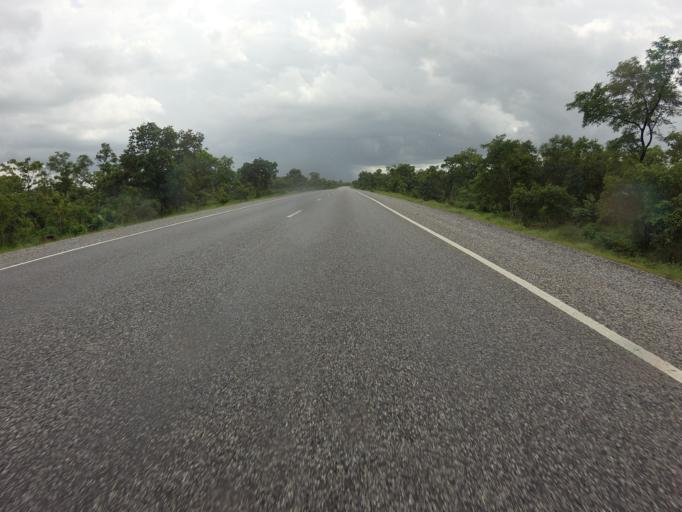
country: GH
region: Northern
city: Tamale
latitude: 9.1449
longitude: -1.3646
